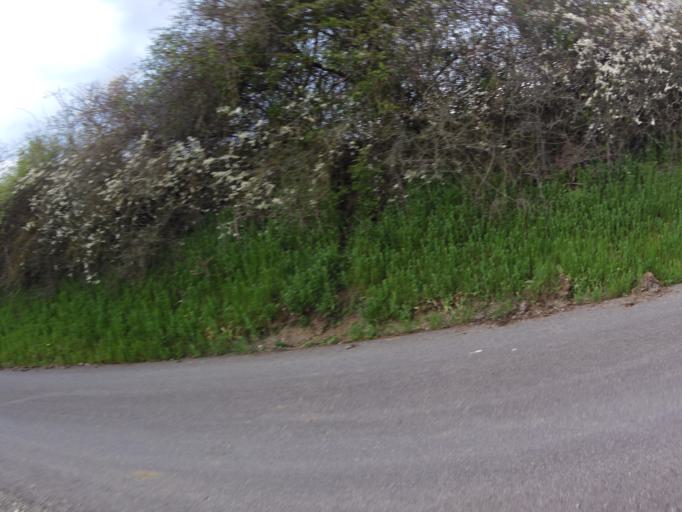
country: DE
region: Bavaria
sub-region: Regierungsbezirk Unterfranken
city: Rimpar
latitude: 49.8604
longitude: 9.9545
